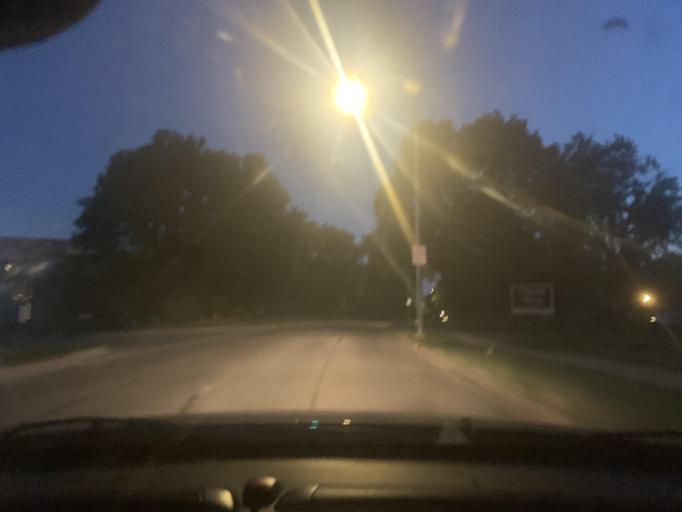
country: US
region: Nebraska
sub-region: Sarpy County
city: La Vista
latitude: 41.1790
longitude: -96.0476
